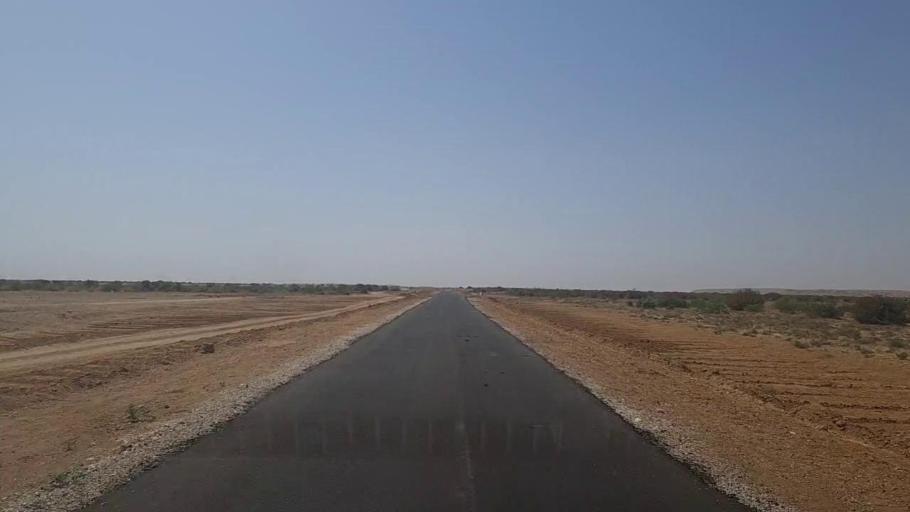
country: PK
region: Sindh
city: Kotri
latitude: 25.1496
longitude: 68.2155
